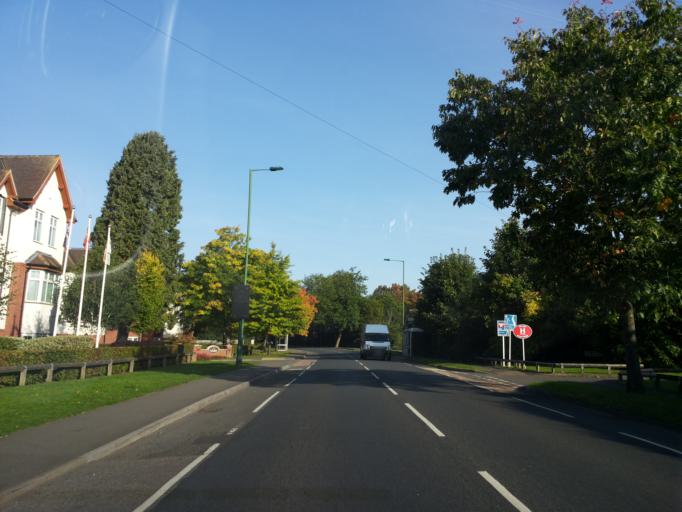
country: GB
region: England
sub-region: Solihull
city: Knowle
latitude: 52.3961
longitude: -1.7423
